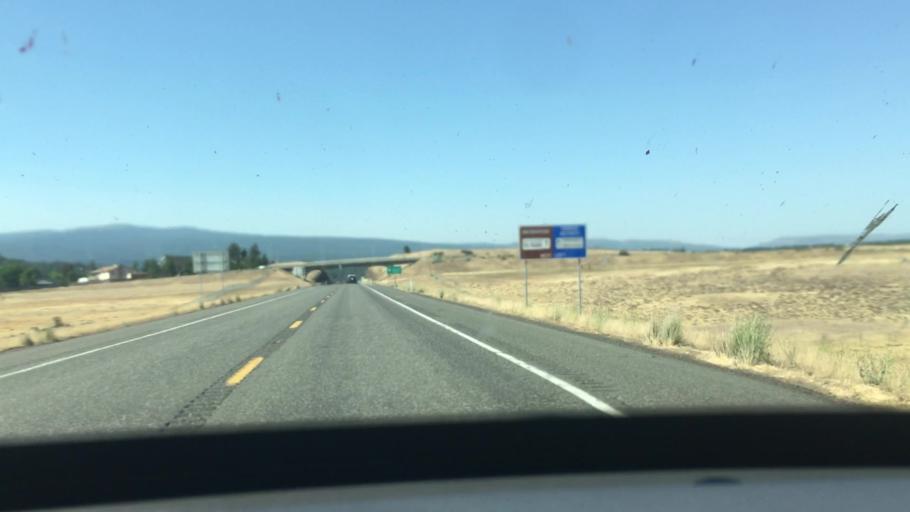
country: US
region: Washington
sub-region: Klickitat County
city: Goldendale
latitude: 45.8156
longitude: -120.8065
